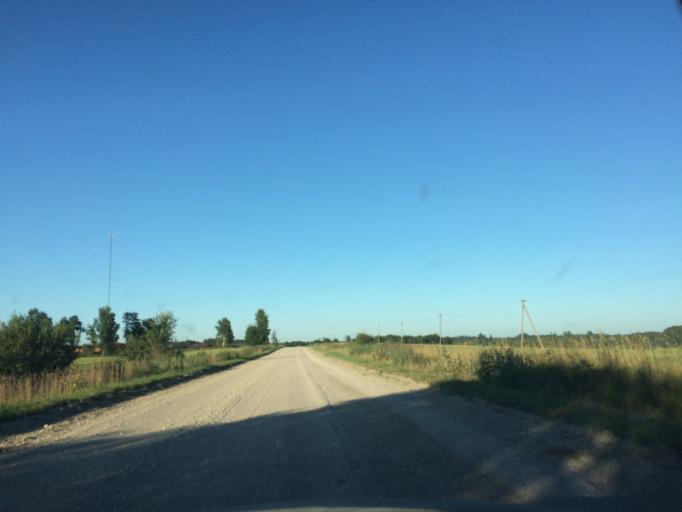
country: LV
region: Rezekne
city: Rezekne
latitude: 56.6174
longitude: 27.4679
